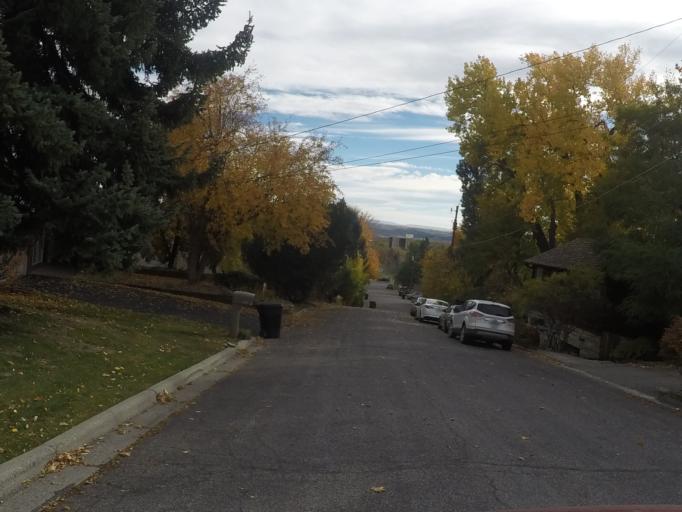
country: US
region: Montana
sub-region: Yellowstone County
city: Billings
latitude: 45.8006
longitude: -108.5499
